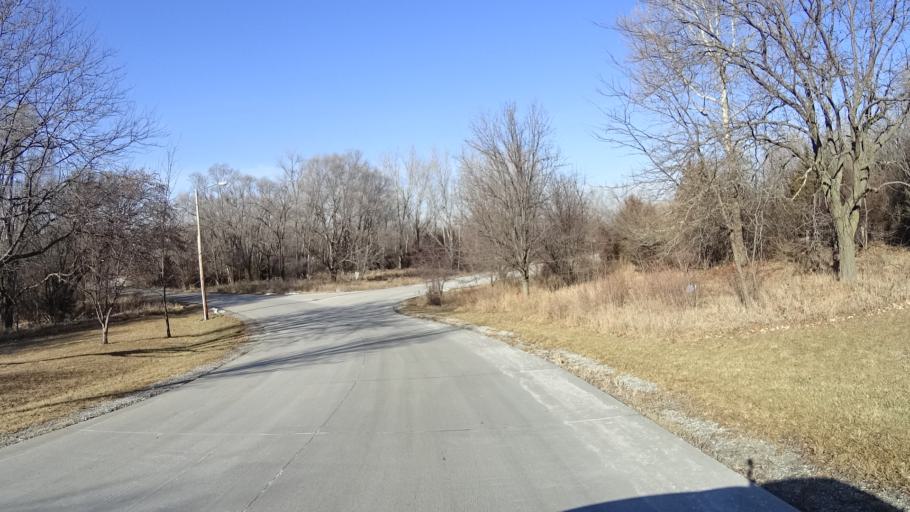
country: US
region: Nebraska
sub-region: Douglas County
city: Bennington
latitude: 41.3074
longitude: -96.1304
